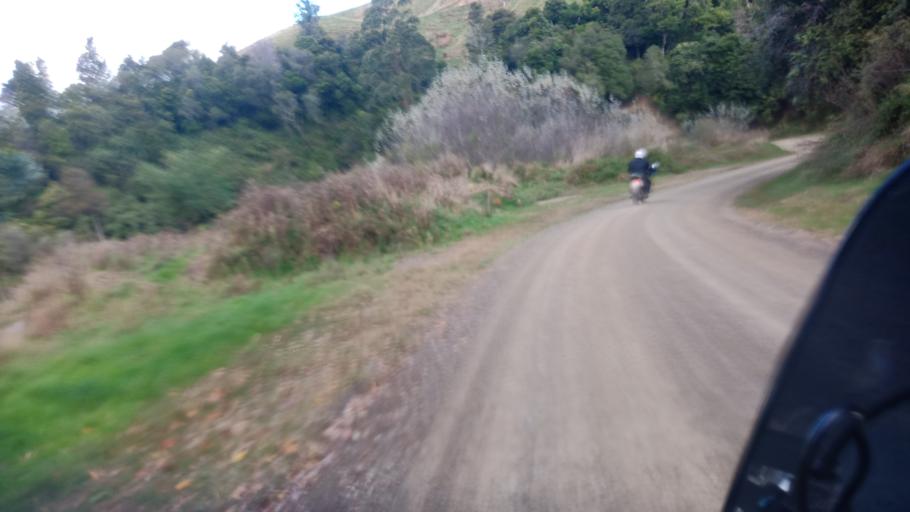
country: NZ
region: Gisborne
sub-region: Gisborne District
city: Gisborne
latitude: -38.4637
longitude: 177.6291
